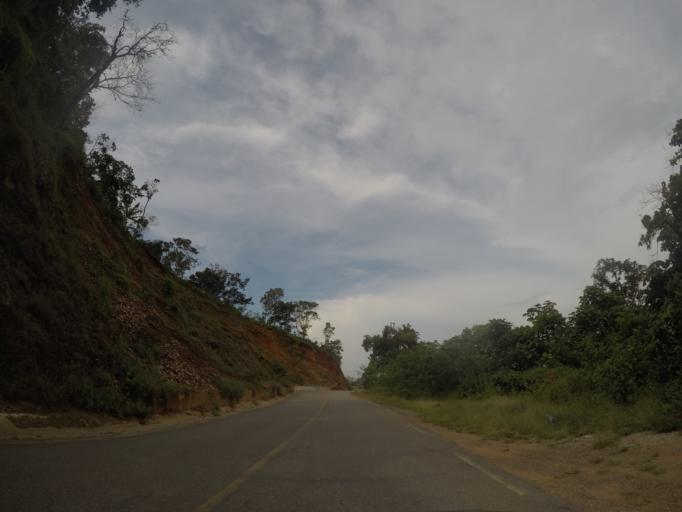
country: MX
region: Oaxaca
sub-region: San Pedro Pochutla
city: Los Naranjos Esquipulas
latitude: 15.9594
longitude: -96.4571
